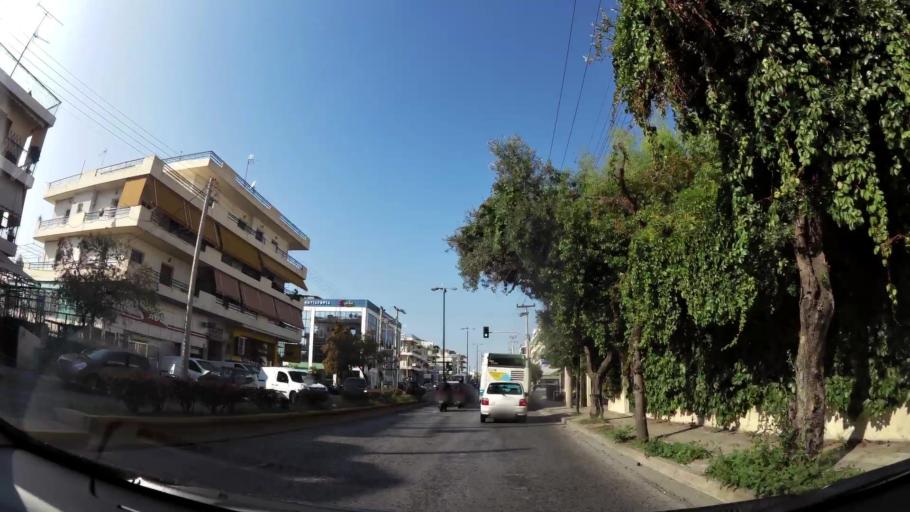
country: GR
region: Attica
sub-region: Nomarchia Athinas
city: Argyroupoli
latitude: 37.9017
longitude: 23.7558
